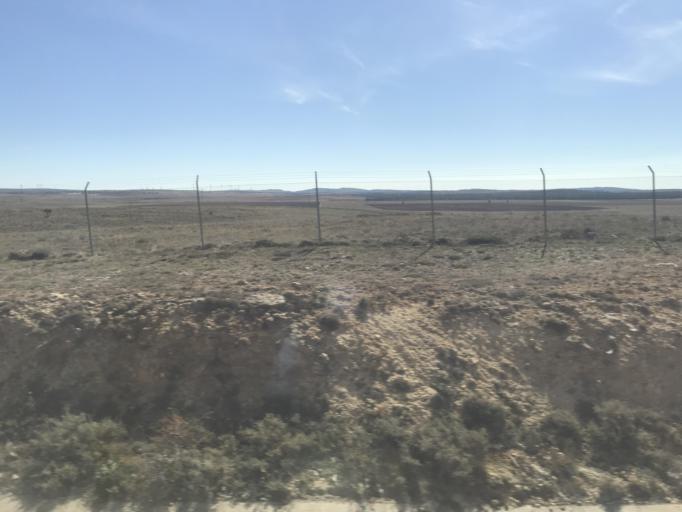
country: ES
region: Castille-La Mancha
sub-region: Provincia de Guadalajara
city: Anguita
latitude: 41.1050
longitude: -2.3734
